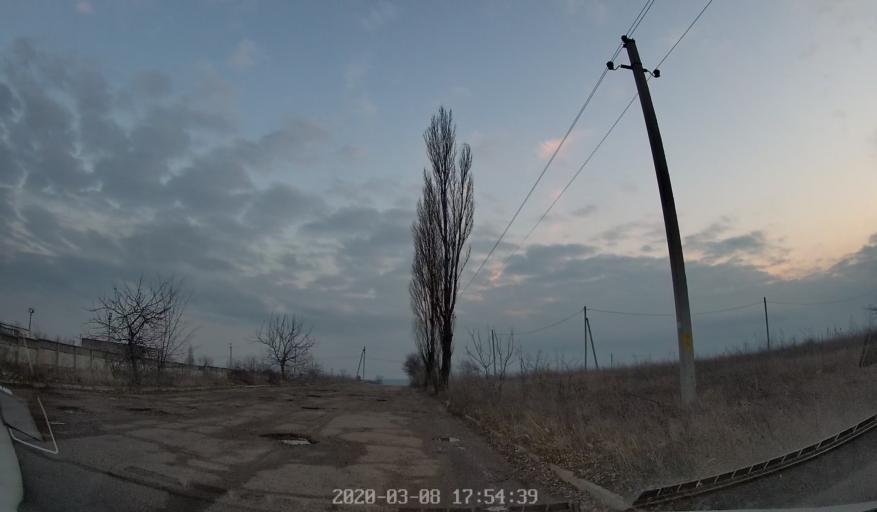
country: MD
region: Rezina
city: Rezina
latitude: 47.7529
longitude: 28.9490
